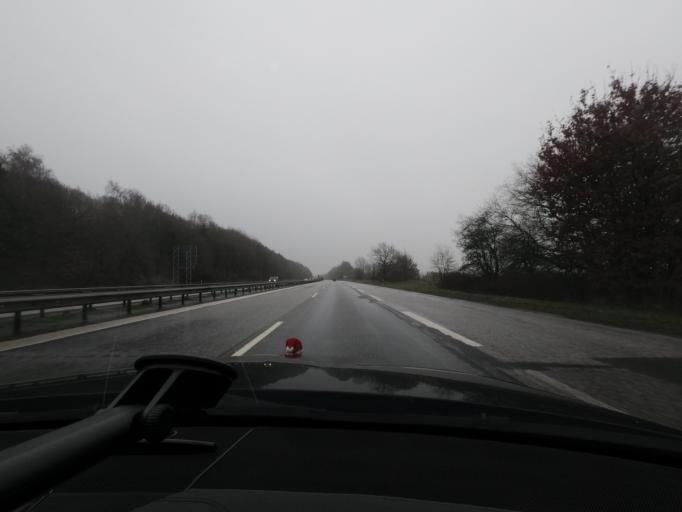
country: DE
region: Schleswig-Holstein
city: Neu Duvenstedt
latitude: 54.3618
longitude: 9.6751
